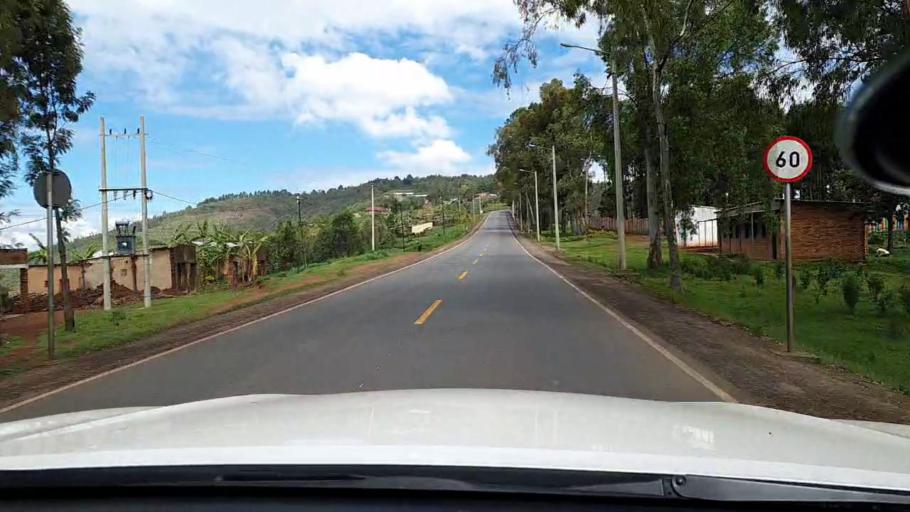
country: RW
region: Kigali
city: Kigali
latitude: -1.8332
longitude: 29.9511
